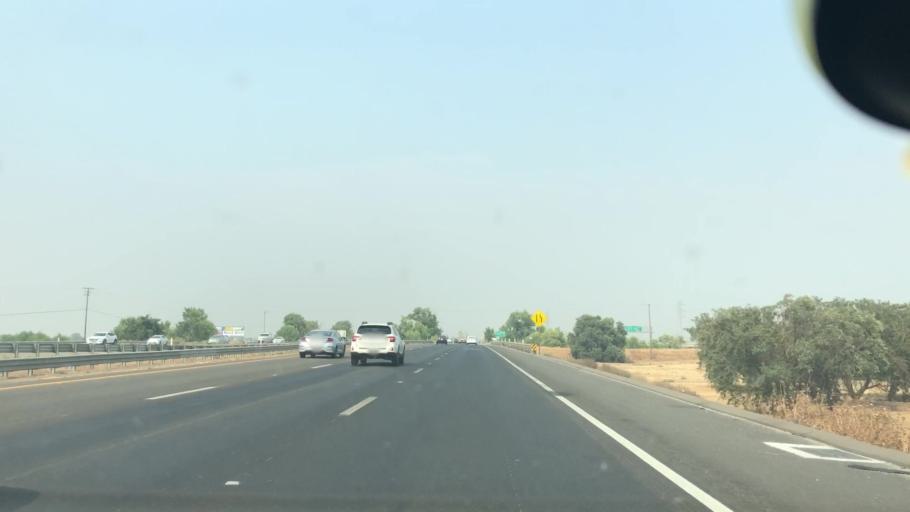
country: US
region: California
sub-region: San Joaquin County
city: Lathrop
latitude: 37.7693
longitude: -121.3286
